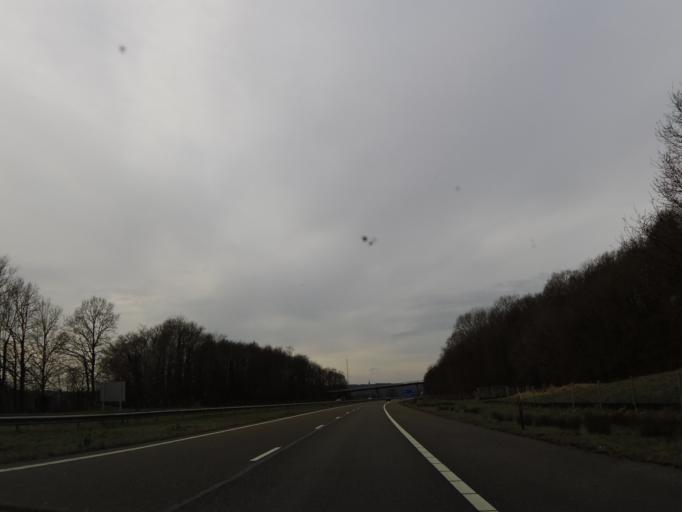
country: NL
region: Limburg
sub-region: Valkenburg aan de Geul
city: Broekhem
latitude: 50.8770
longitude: 5.8273
